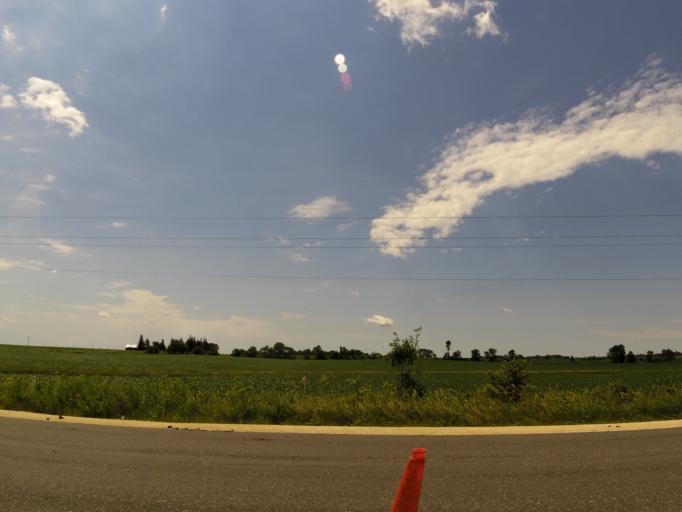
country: US
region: Iowa
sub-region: Bremer County
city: Denver
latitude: 42.7151
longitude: -92.3202
